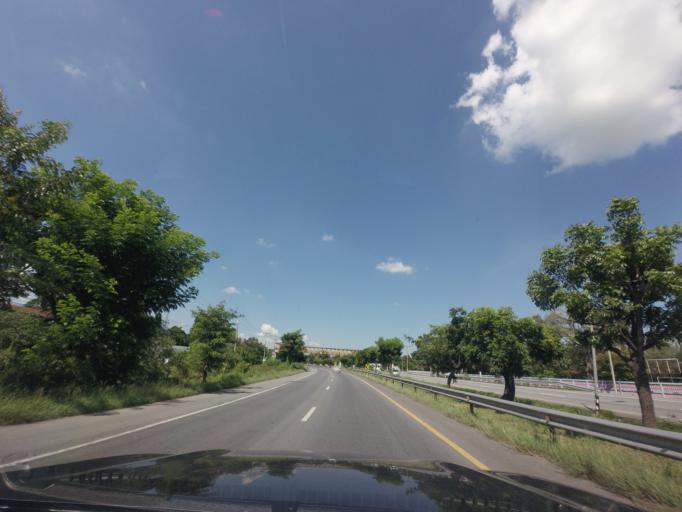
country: TH
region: Nakhon Ratchasima
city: Non Sung
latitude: 15.1469
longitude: 102.3242
